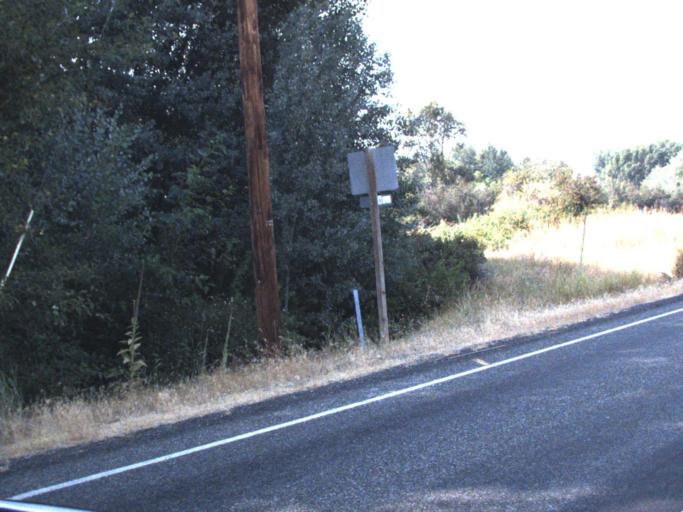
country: US
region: Washington
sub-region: Kittitas County
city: Ellensburg
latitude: 46.9255
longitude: -120.5099
